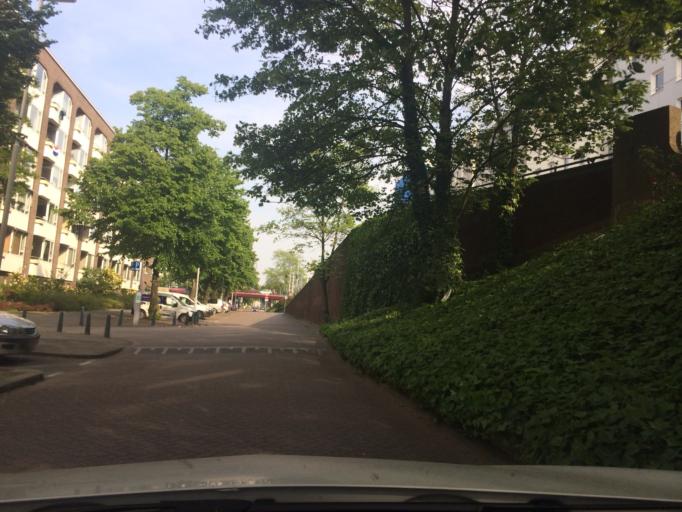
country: NL
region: South Holland
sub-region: Gemeente Rotterdam
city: Rotterdam
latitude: 51.9222
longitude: 4.5040
